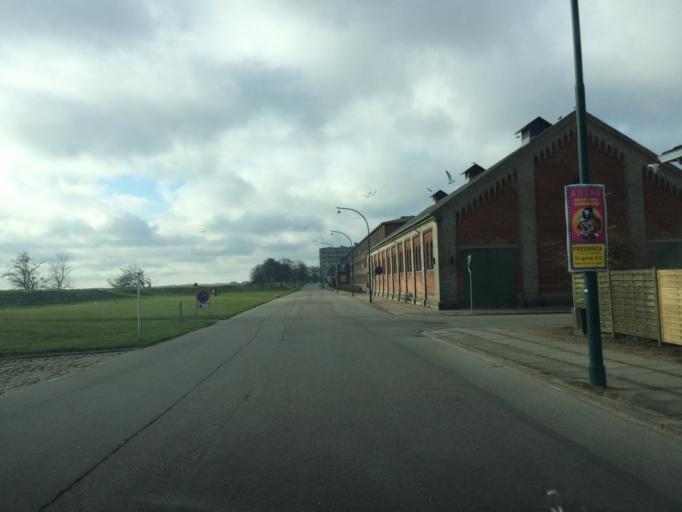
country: DK
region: South Denmark
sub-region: Fredericia Kommune
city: Fredericia
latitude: 55.5673
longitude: 9.7677
